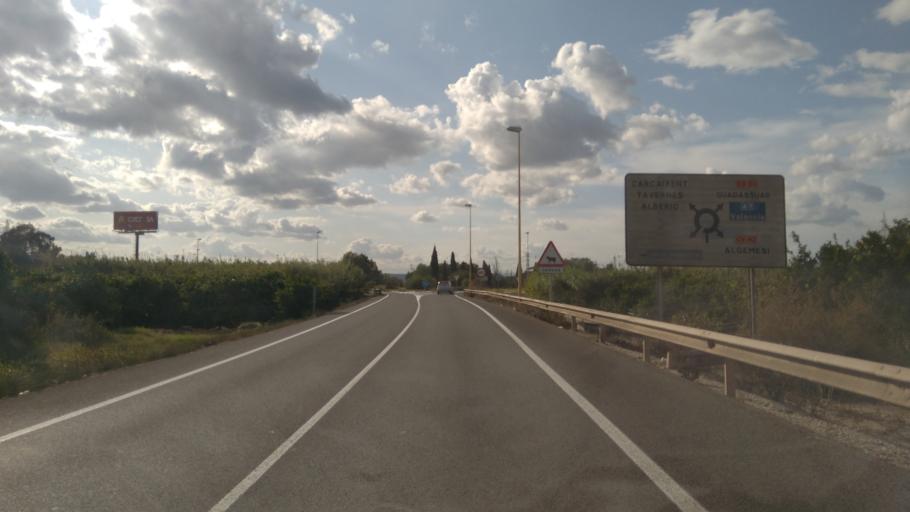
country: ES
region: Valencia
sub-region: Provincia de Valencia
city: Alzira
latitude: 39.1637
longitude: -0.4434
